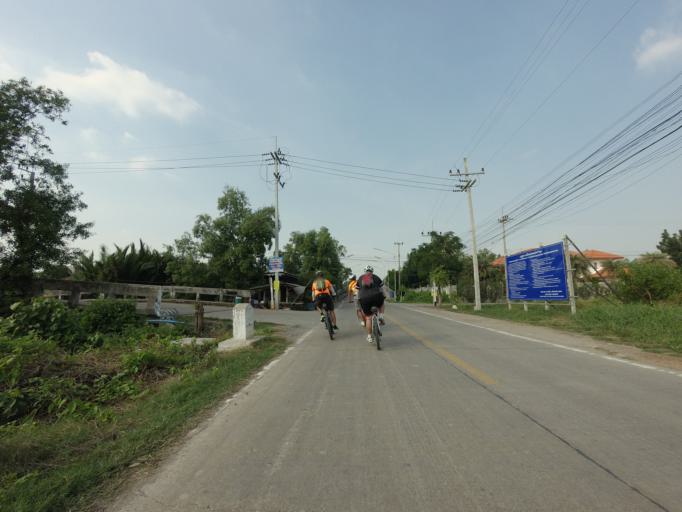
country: TH
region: Samut Sakhon
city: Samut Sakhon
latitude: 13.5121
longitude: 100.3069
